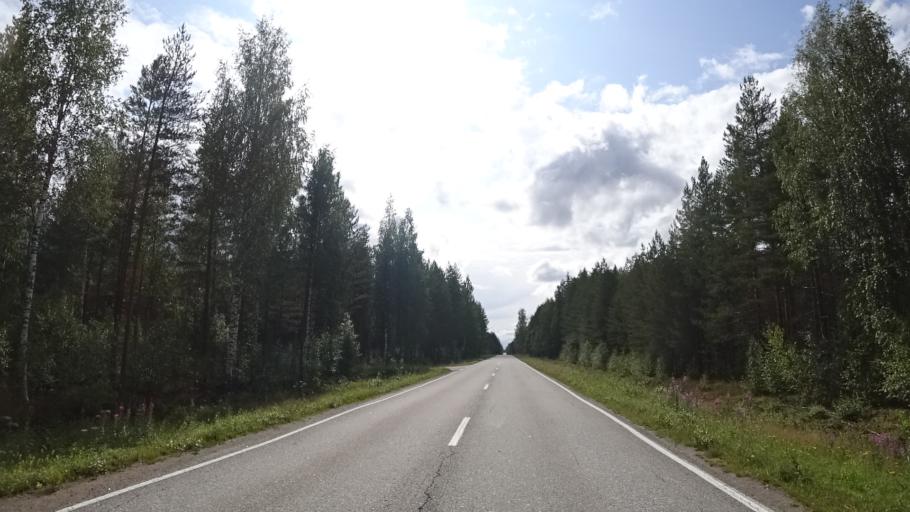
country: FI
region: North Karelia
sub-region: Joensuu
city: Ilomantsi
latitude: 62.7624
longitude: 31.0219
